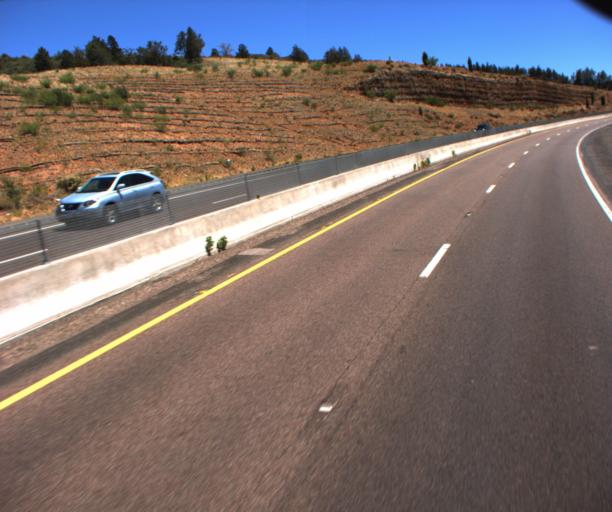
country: US
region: Arizona
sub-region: Gila County
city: Tonto Basin
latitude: 33.9390
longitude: -111.4406
